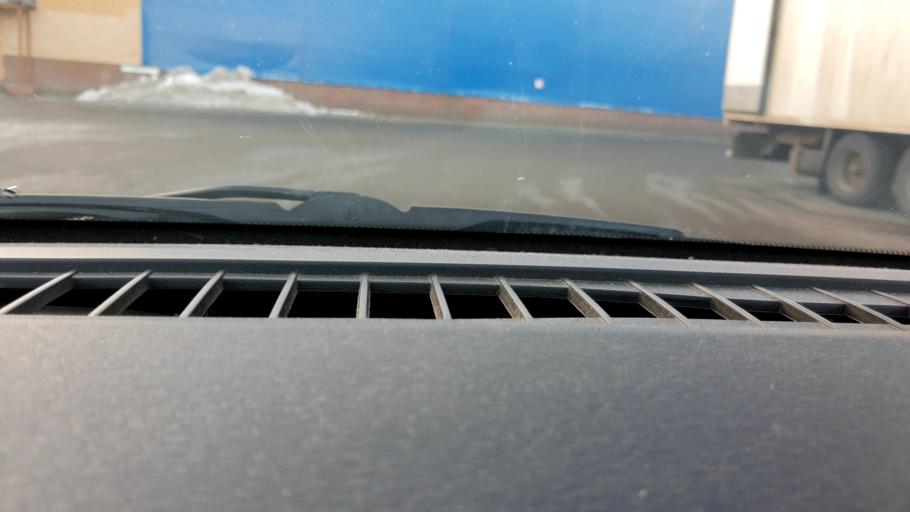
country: RU
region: Nizjnij Novgorod
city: Nizhniy Novgorod
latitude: 56.2591
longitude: 43.9184
